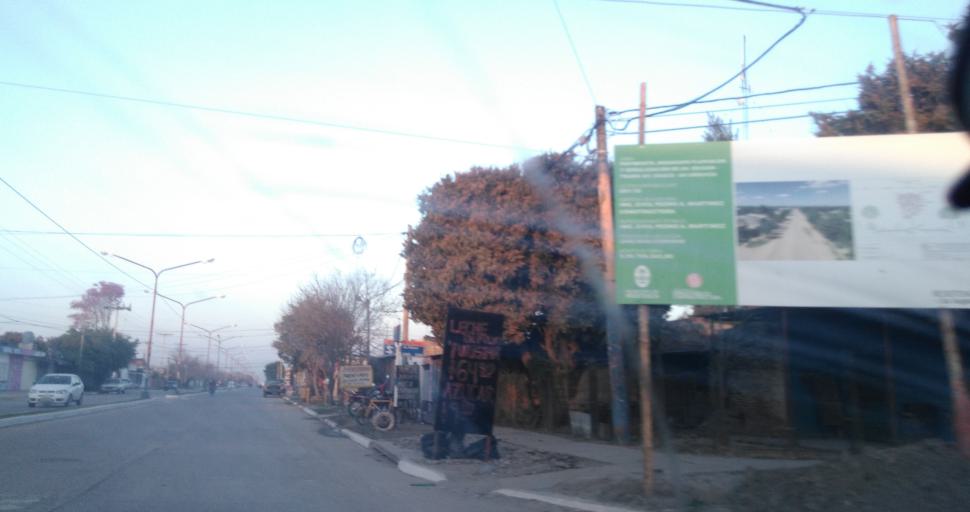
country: AR
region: Chaco
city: Resistencia
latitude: -27.4830
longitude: -58.9793
